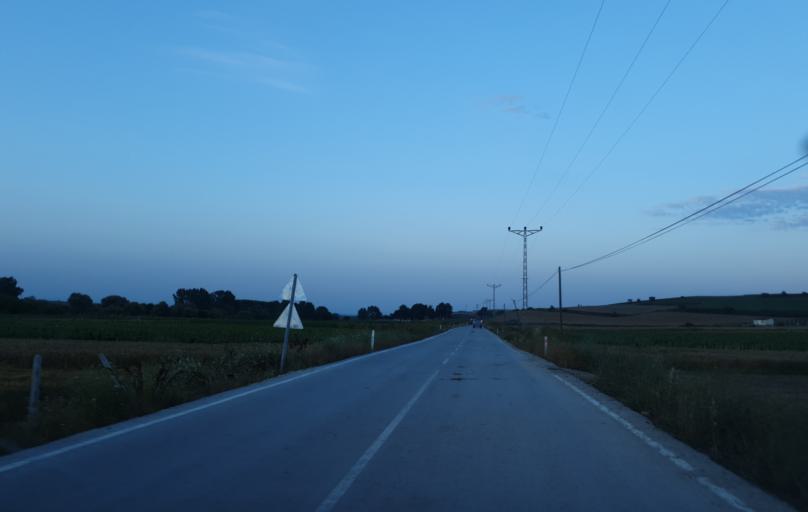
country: TR
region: Tekirdag
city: Velimese
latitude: 41.3481
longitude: 27.8700
